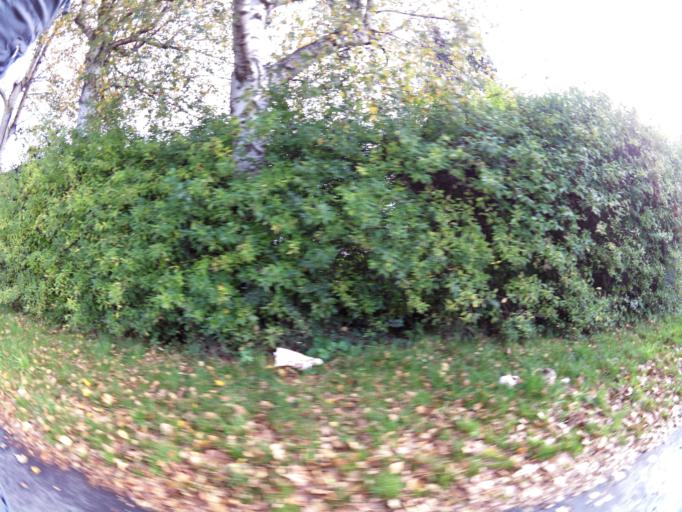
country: NO
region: Ostfold
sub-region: Fredrikstad
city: Fredrikstad
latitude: 59.2207
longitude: 10.9089
